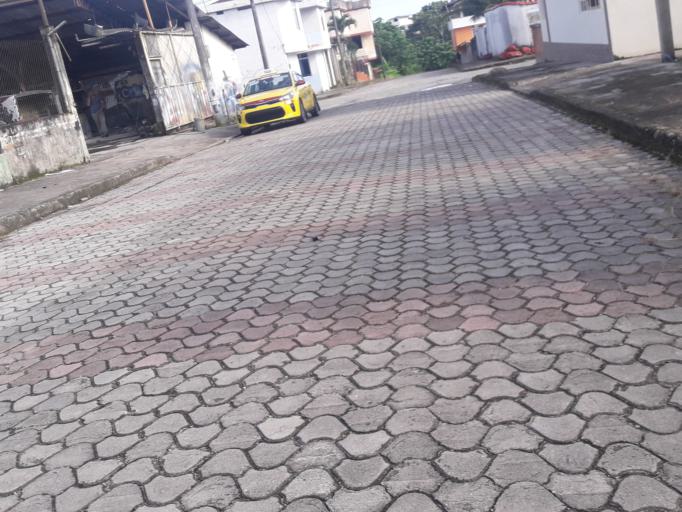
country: EC
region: Napo
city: Tena
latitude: -0.9838
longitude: -77.8117
